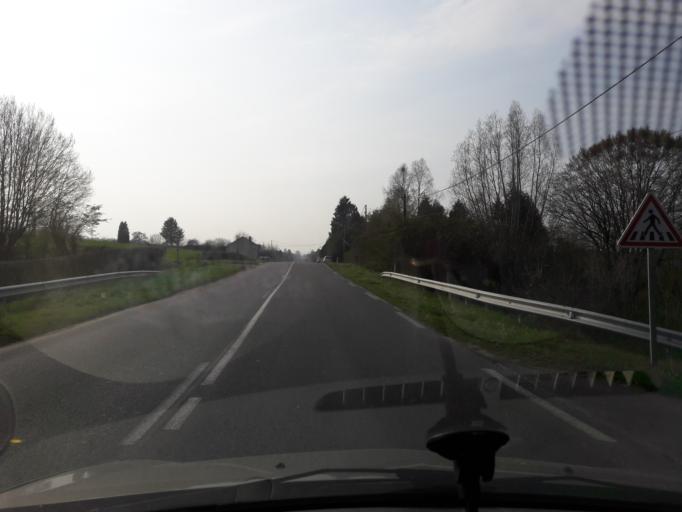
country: FR
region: Nord-Pas-de-Calais
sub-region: Departement du Nord
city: Marpent
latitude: 50.2518
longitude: 4.0941
